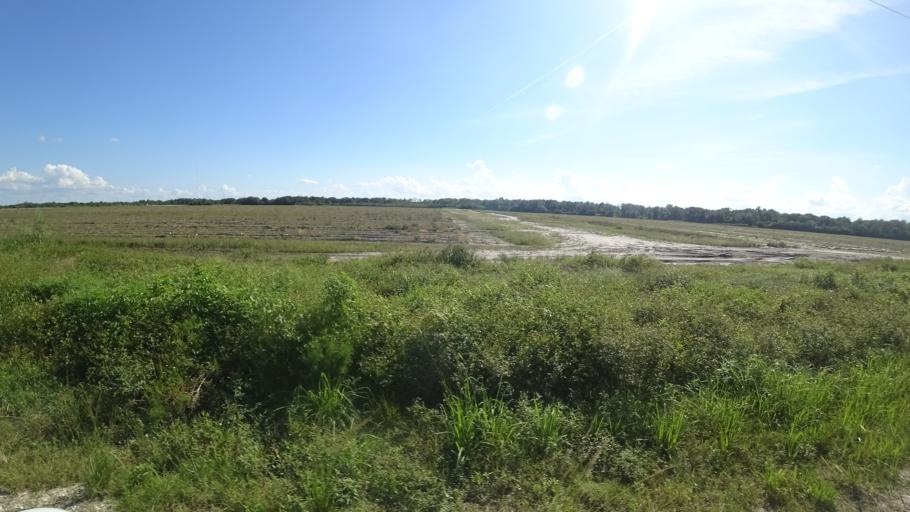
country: US
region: Florida
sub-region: Sarasota County
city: The Meadows
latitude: 27.4450
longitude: -82.2767
